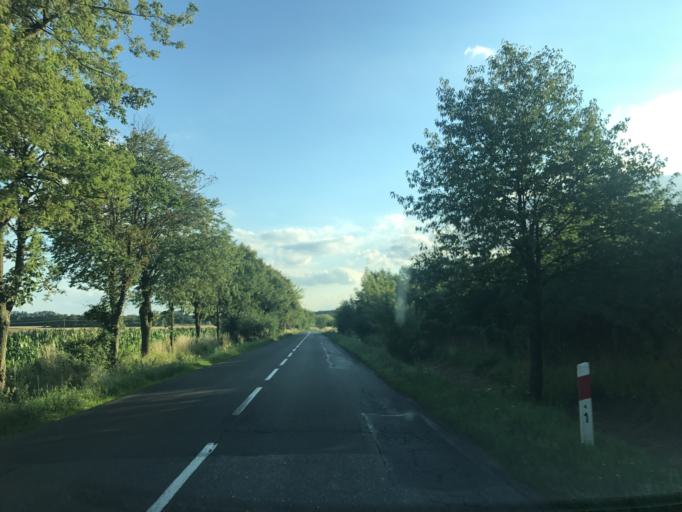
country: PL
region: Greater Poland Voivodeship
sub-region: Powiat jarocinski
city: Witaszyce
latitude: 51.9912
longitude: 17.5556
